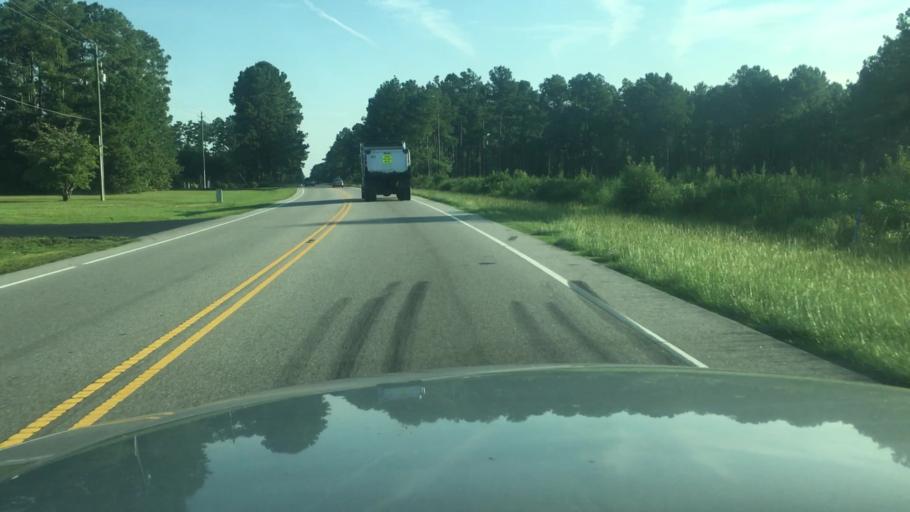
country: US
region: North Carolina
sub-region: Harnett County
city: Walkertown
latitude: 35.1944
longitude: -78.8496
